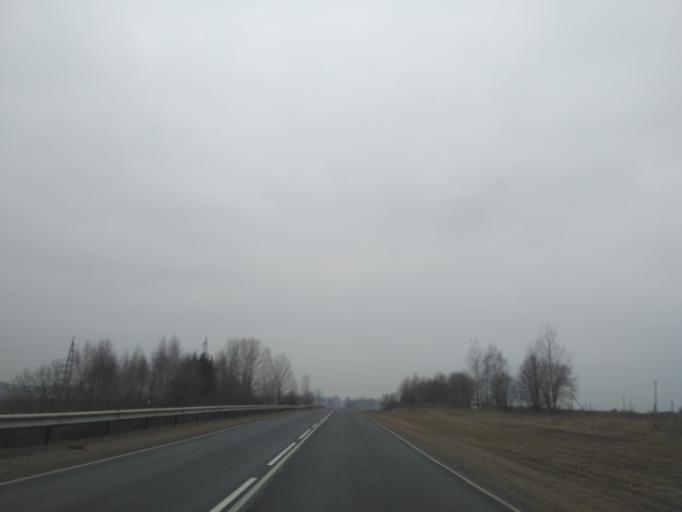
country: BY
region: Brest
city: Baranovichi
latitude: 53.1776
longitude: 26.0565
